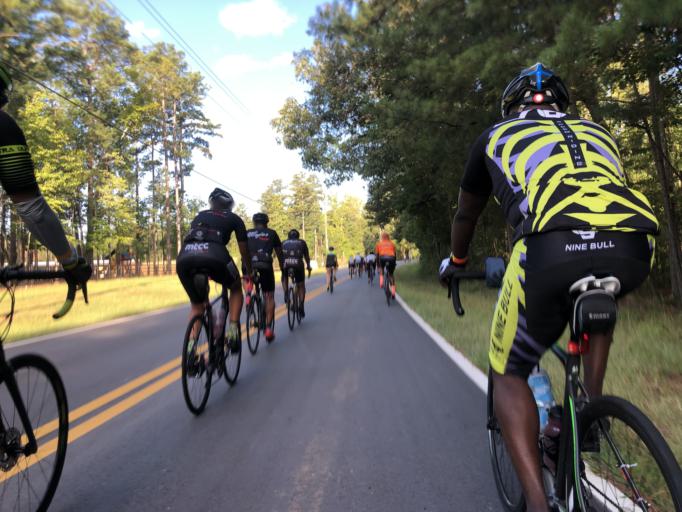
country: US
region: Georgia
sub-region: Fulton County
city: Chattahoochee Hills
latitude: 33.5821
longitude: -84.7006
